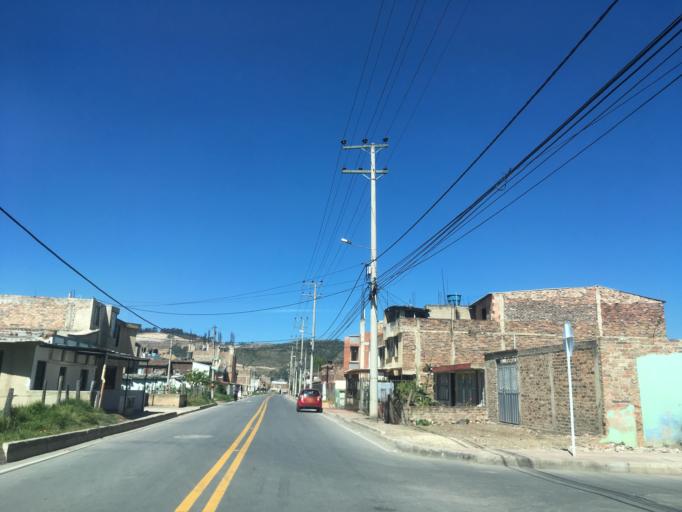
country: CO
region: Boyaca
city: Sogamoso
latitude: 5.7096
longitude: -72.9425
